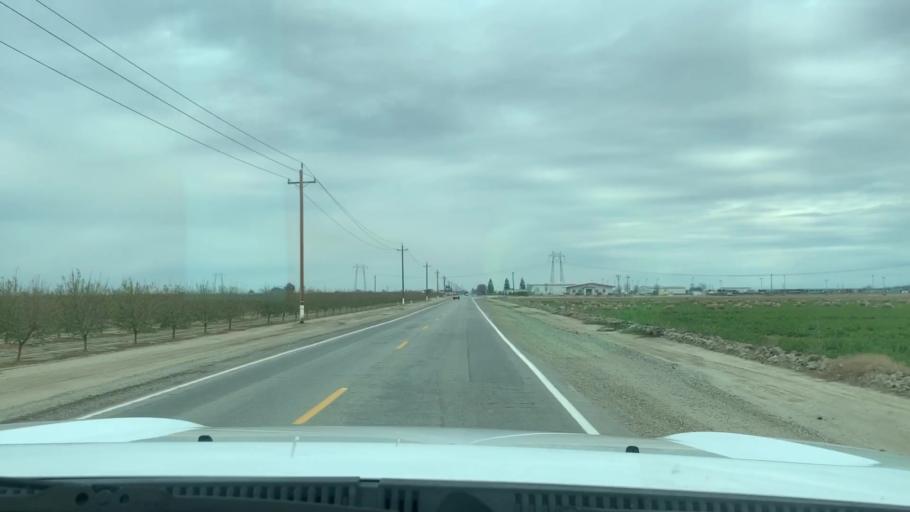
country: US
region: California
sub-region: Kern County
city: Rosedale
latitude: 35.3584
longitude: -119.2521
